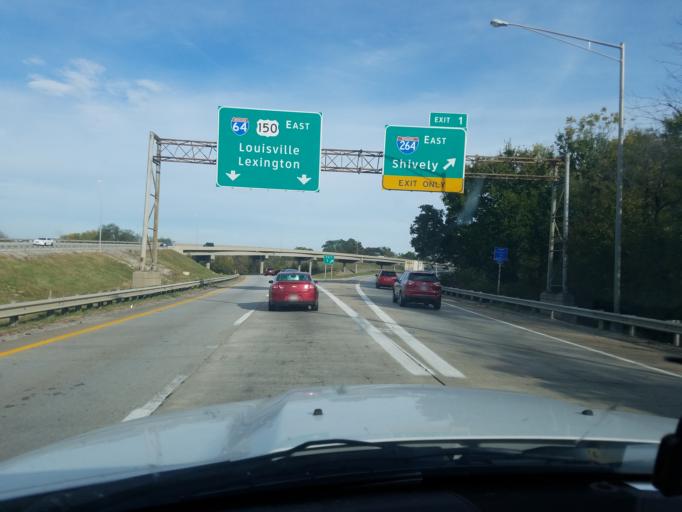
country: US
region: Indiana
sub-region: Floyd County
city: New Albany
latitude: 38.2751
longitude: -85.8134
